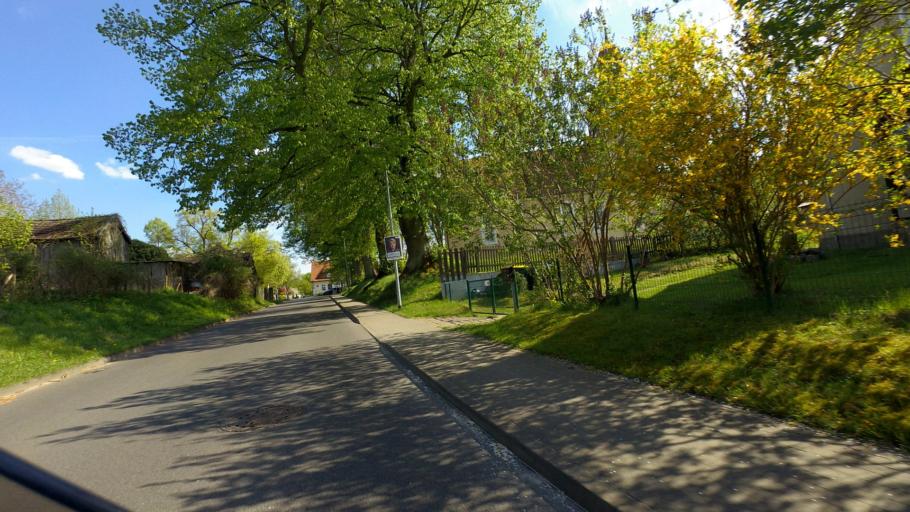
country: DE
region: Brandenburg
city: Templin
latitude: 53.0514
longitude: 13.5296
